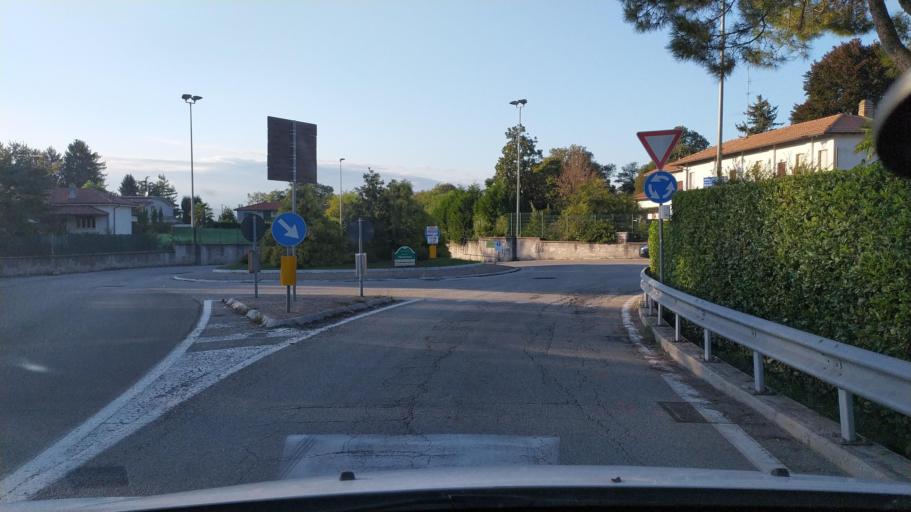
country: IT
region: Lombardy
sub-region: Provincia di Varese
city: Golasecca
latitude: 45.7017
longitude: 8.6615
